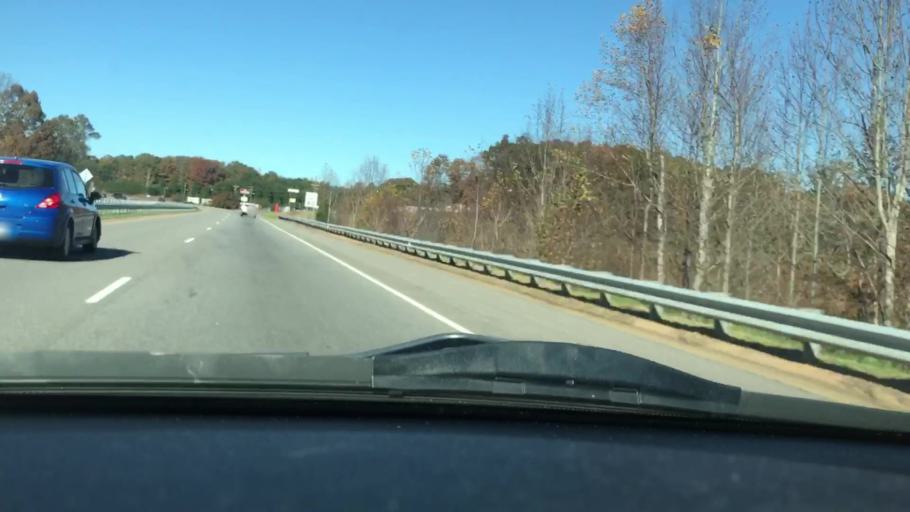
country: US
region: North Carolina
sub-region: Rockingham County
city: Stoneville
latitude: 36.4762
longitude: -79.9248
